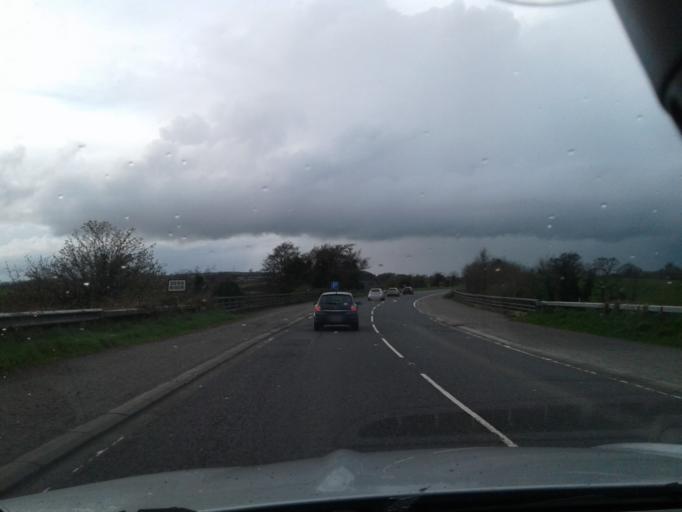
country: GB
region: Northern Ireland
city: Newtownstewart
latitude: 54.7360
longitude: -7.4319
